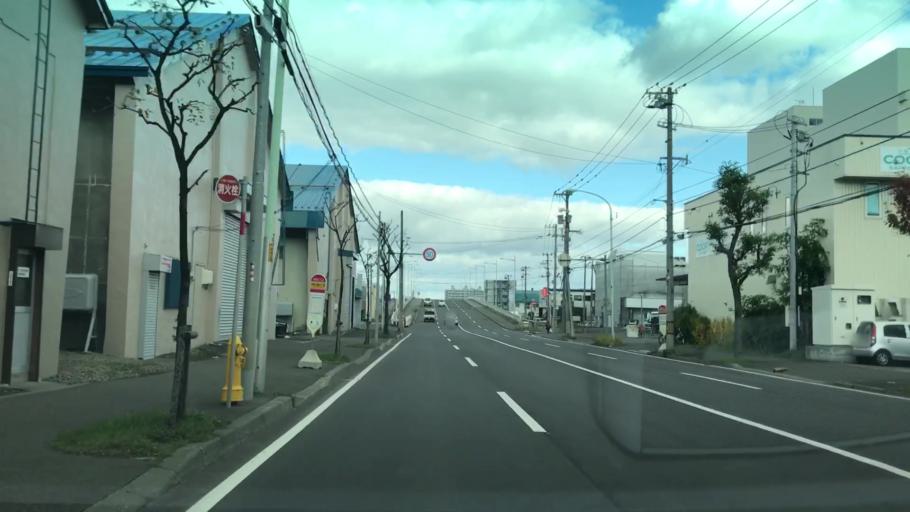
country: JP
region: Hokkaido
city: Sapporo
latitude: 43.0596
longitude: 141.4002
